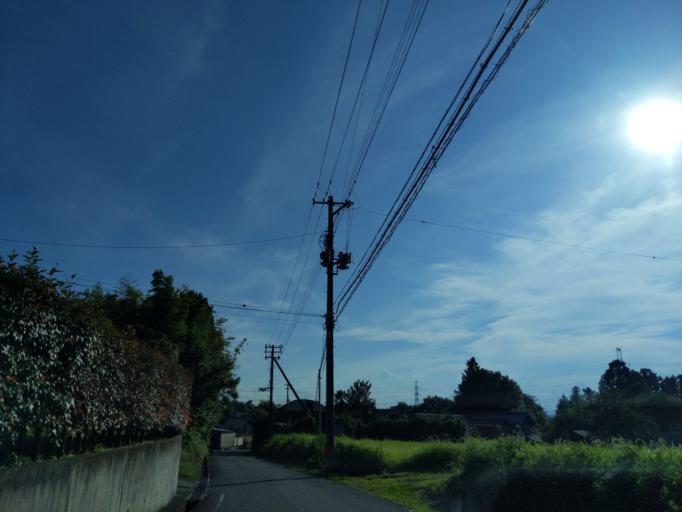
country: JP
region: Fukushima
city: Sukagawa
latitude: 37.3203
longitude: 140.4329
